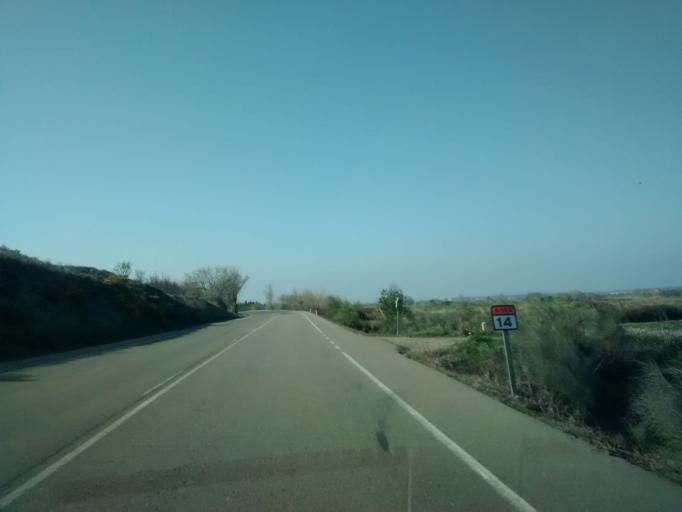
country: ES
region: Aragon
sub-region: Provincia de Zaragoza
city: Villanueva de Gallego
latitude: 41.7807
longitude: -0.7882
